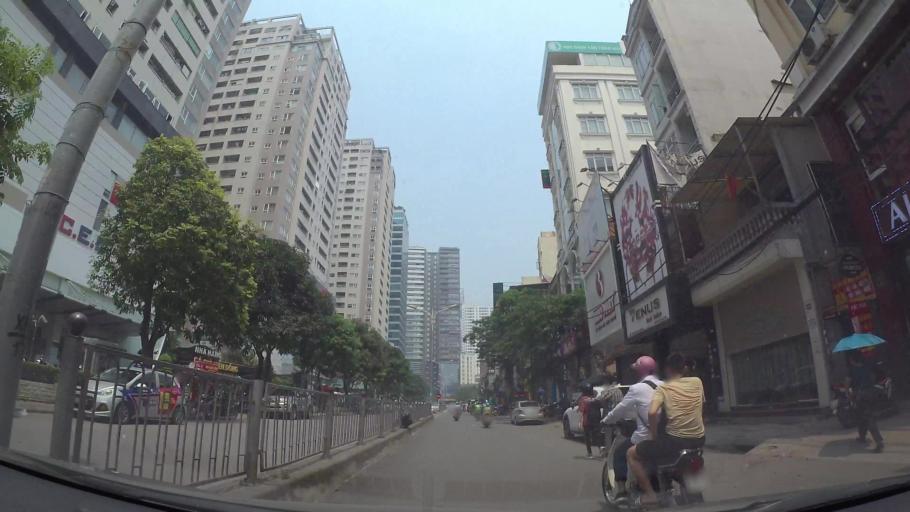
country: VN
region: Ha Noi
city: Thanh Xuan
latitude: 21.0008
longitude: 105.8071
